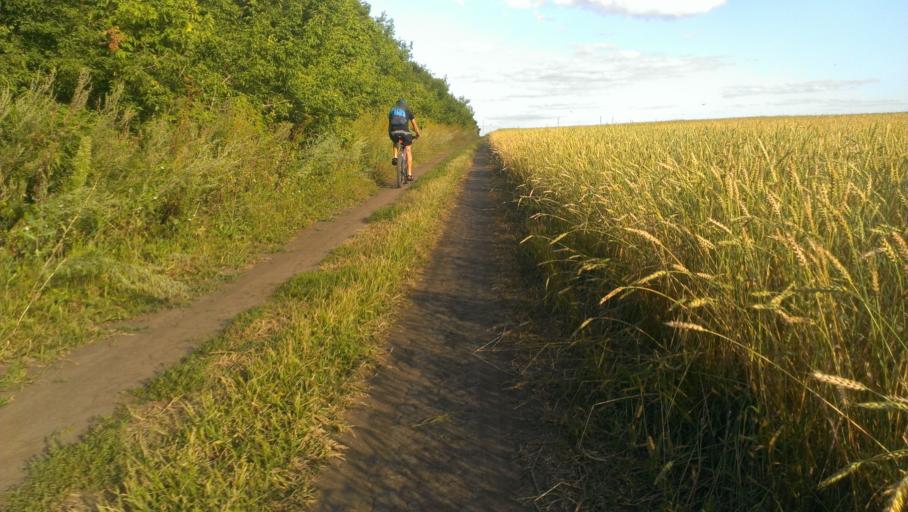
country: RU
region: Altai Krai
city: Gon'ba
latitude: 53.3852
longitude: 83.6033
